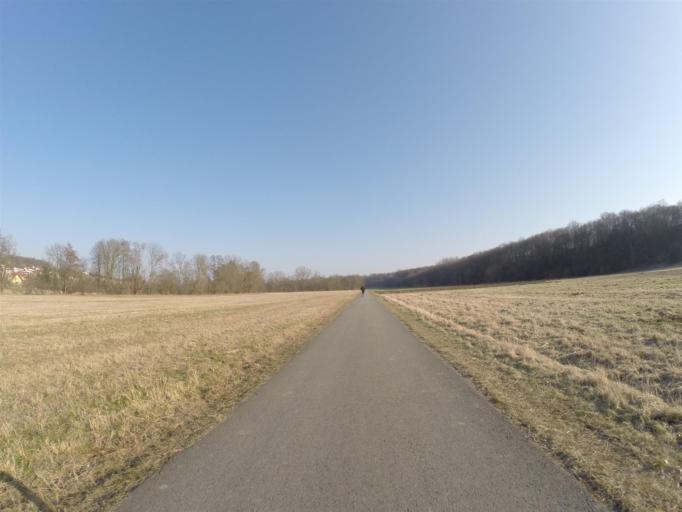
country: DE
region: Thuringia
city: Vollersroda
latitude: 50.9574
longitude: 11.3553
